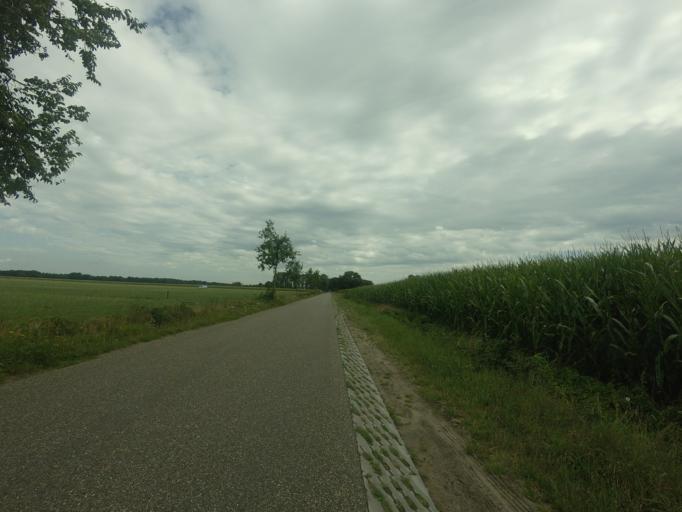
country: NL
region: Overijssel
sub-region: Gemeente Dalfsen
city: Dalfsen
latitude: 52.4767
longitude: 6.3677
